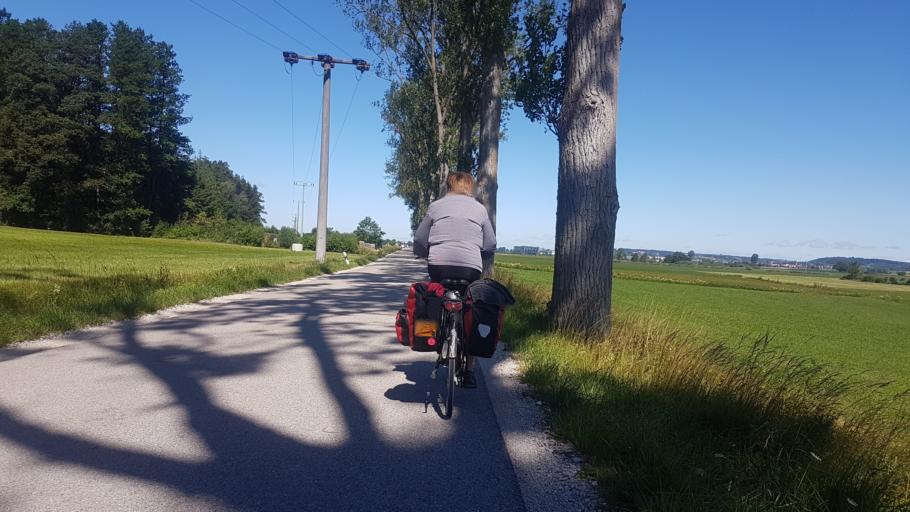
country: DE
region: Bavaria
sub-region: Regierungsbezirk Mittelfranken
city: Burgoberbach
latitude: 49.2074
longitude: 10.5425
